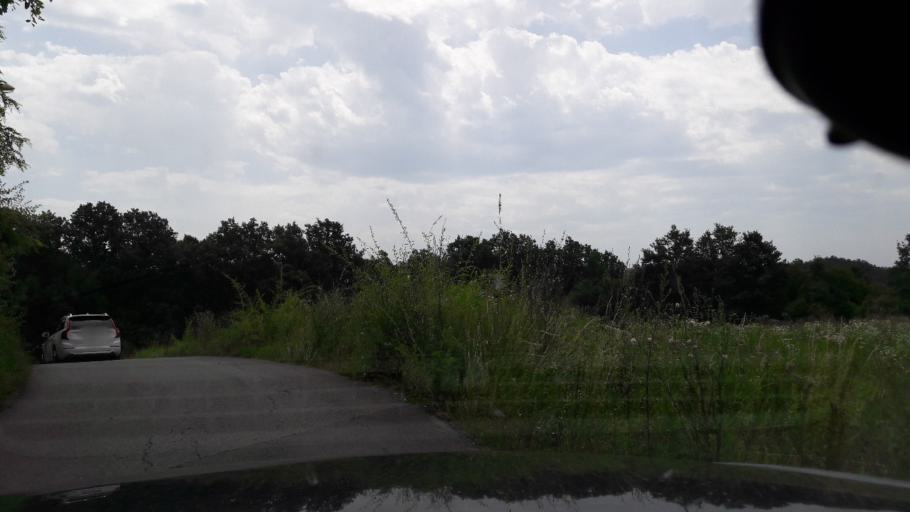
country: RS
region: Central Serbia
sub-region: Belgrade
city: Sopot
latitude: 44.6372
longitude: 20.5931
